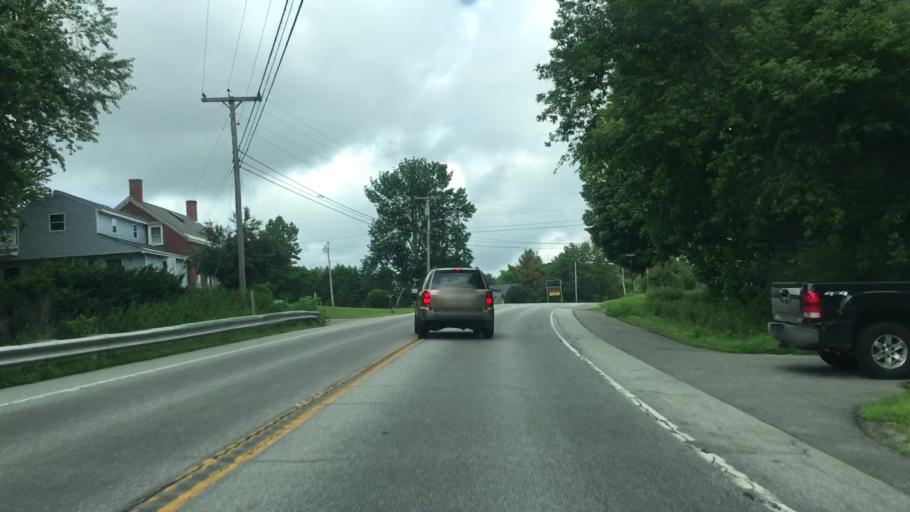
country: US
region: Maine
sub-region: Kennebec County
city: Hallowell
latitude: 44.2819
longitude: -69.7767
